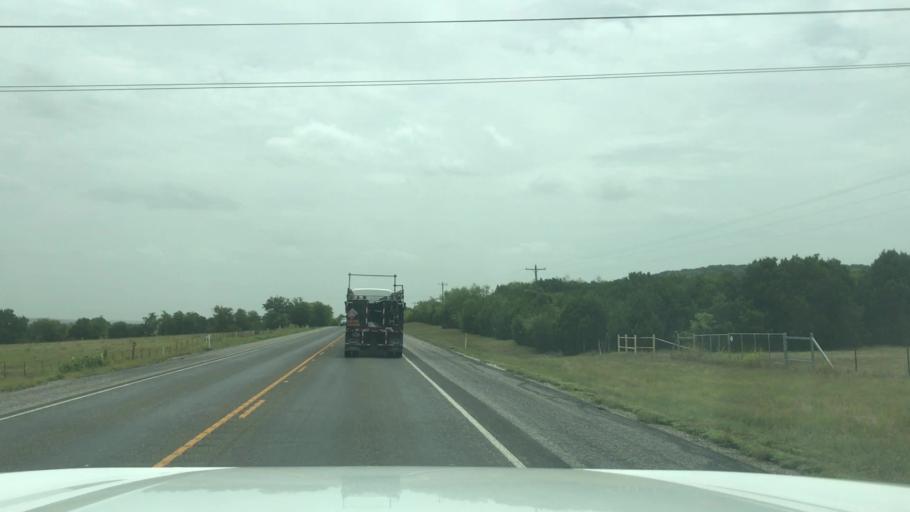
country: US
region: Texas
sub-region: Bosque County
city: Meridian
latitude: 31.8726
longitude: -97.6380
